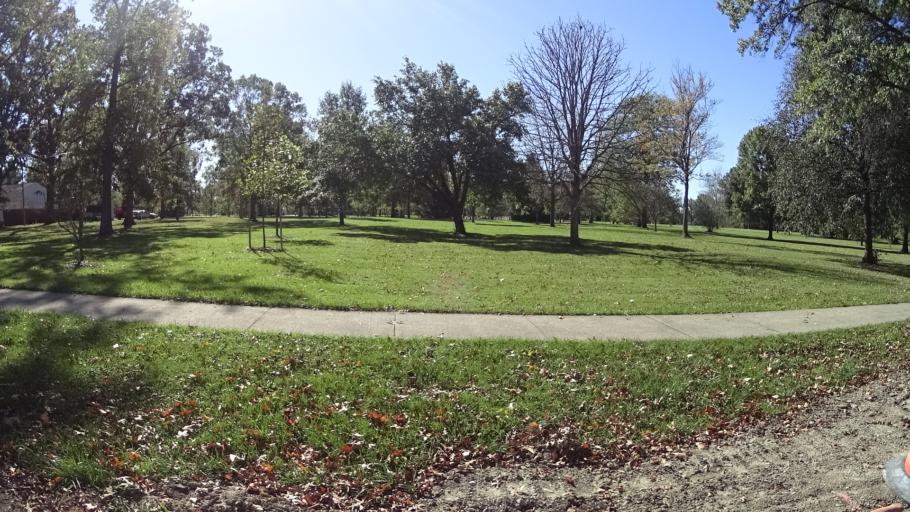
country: US
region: Ohio
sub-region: Lorain County
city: Oberlin
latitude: 41.2871
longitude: -82.2347
